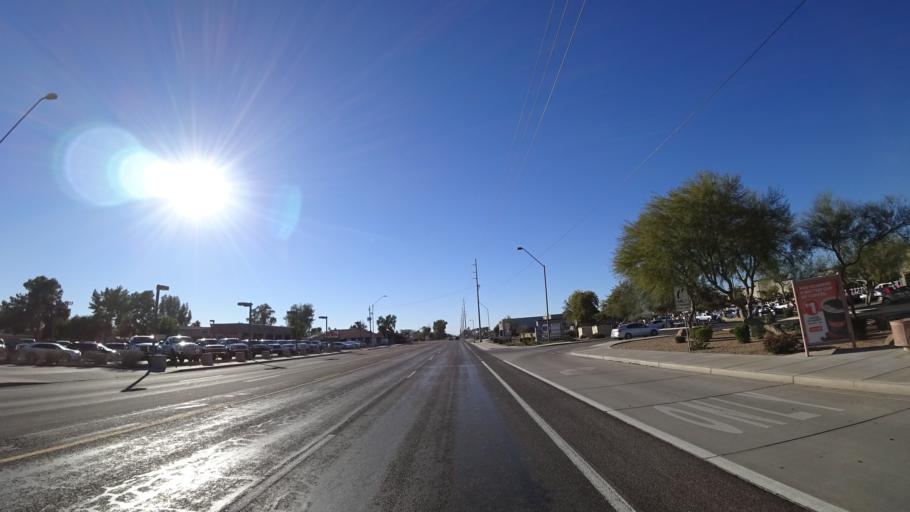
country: US
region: Arizona
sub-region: Maricopa County
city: Avondale
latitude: 33.4499
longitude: -112.3501
